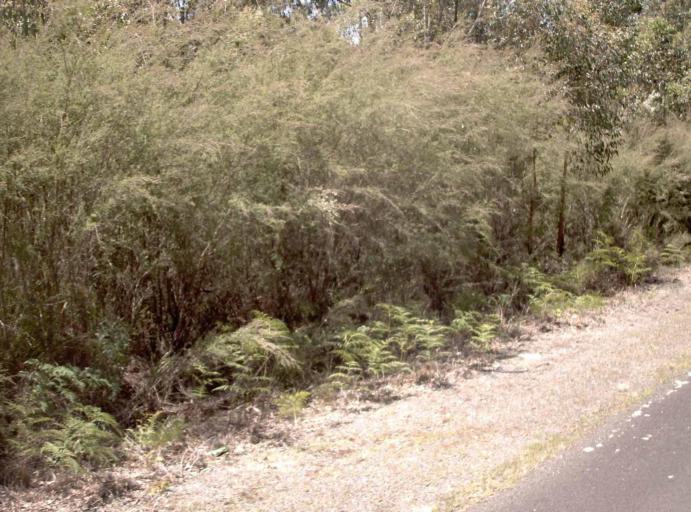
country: AU
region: Victoria
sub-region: East Gippsland
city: Lakes Entrance
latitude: -37.7087
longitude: 148.6928
